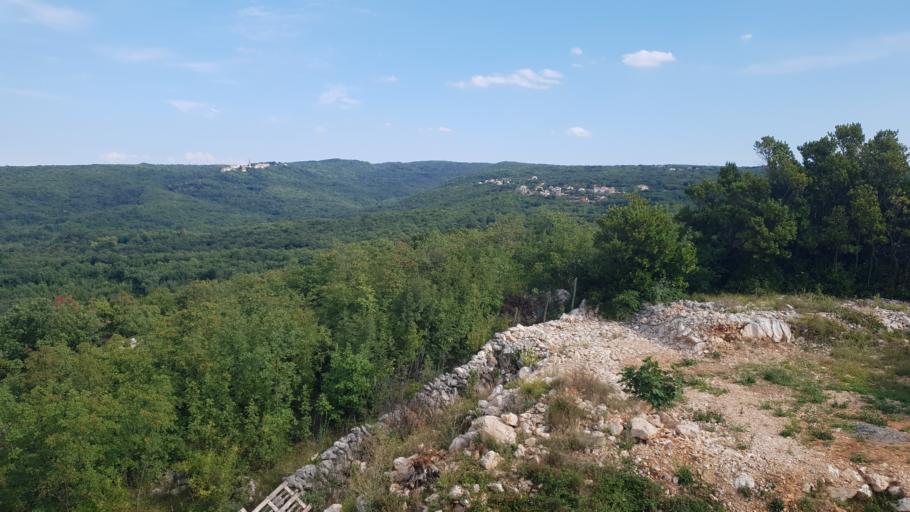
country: HR
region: Primorsko-Goranska
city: Njivice
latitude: 45.1492
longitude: 14.5811
